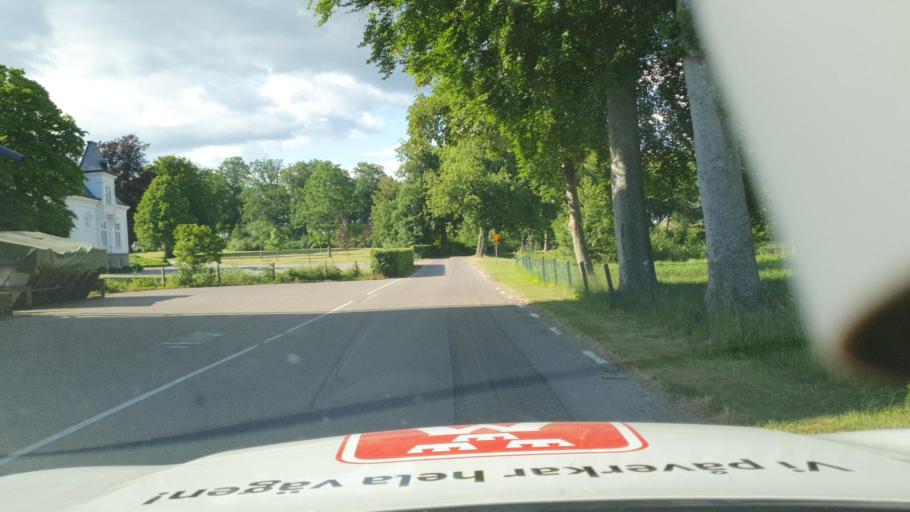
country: SE
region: Skane
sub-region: Ystads Kommun
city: Ystad
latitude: 55.4454
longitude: 13.7351
